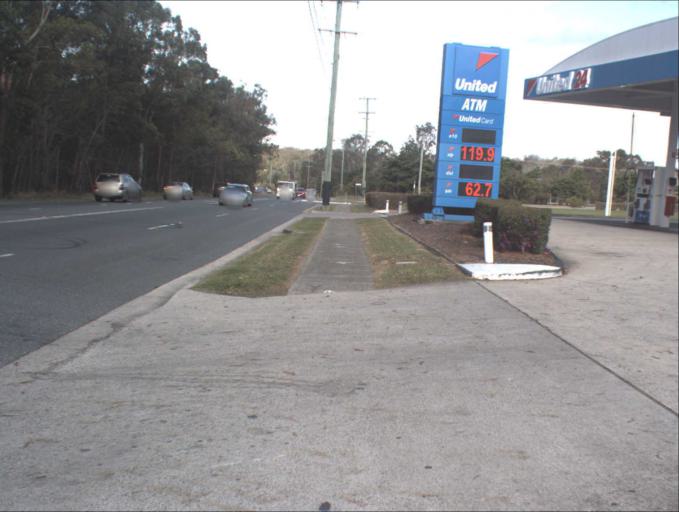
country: AU
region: Queensland
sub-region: Brisbane
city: Forest Lake
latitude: -27.6537
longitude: 152.9955
